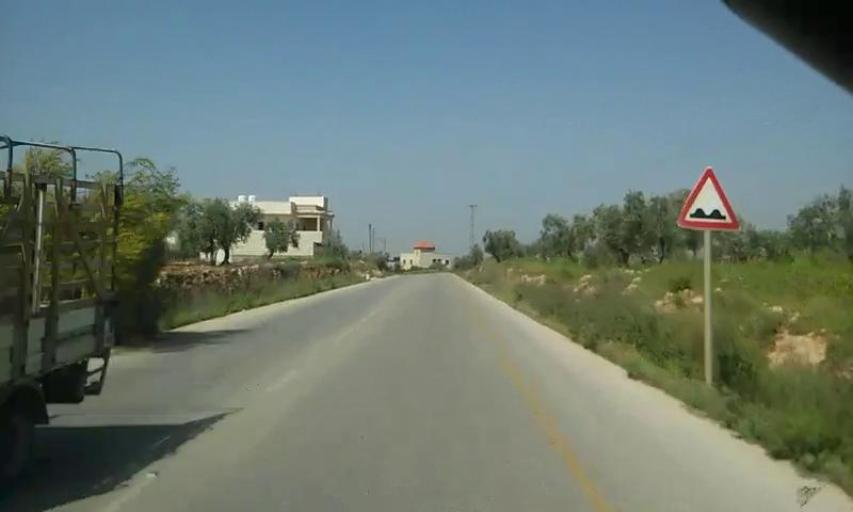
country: PS
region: West Bank
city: Az Zababidah
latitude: 32.3801
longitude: 35.3307
